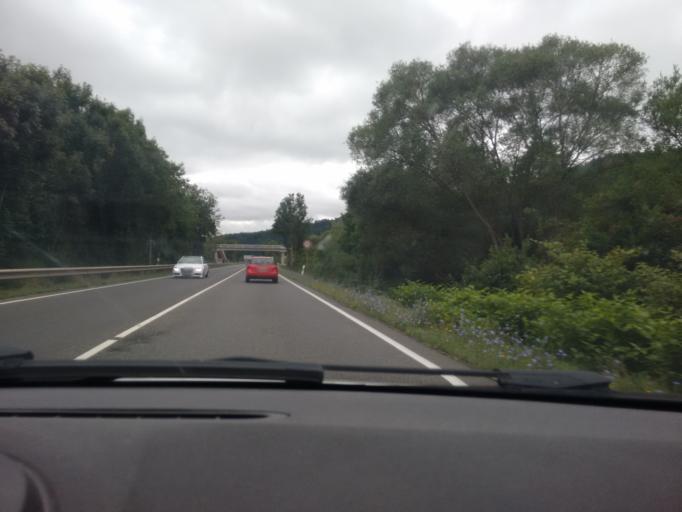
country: DE
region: Rheinland-Pfalz
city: Hintertiefenbach
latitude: 49.7158
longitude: 7.3691
